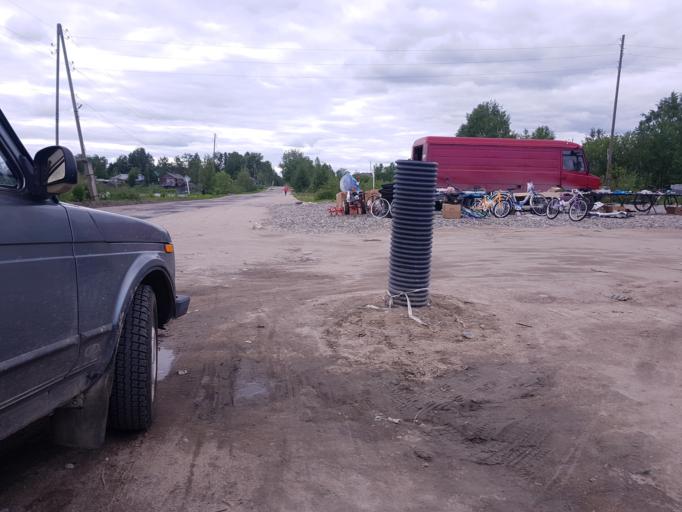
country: RU
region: Republic of Karelia
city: Kalevala
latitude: 65.1985
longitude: 31.1797
